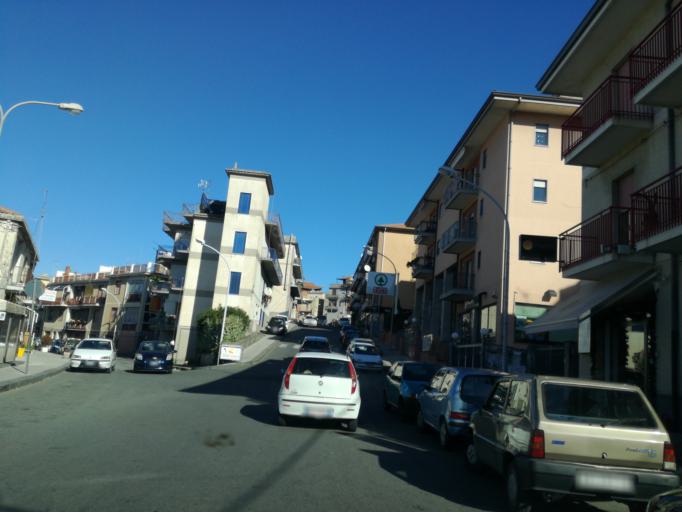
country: IT
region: Sicily
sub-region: Catania
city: Bronte
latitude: 37.7845
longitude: 14.8373
